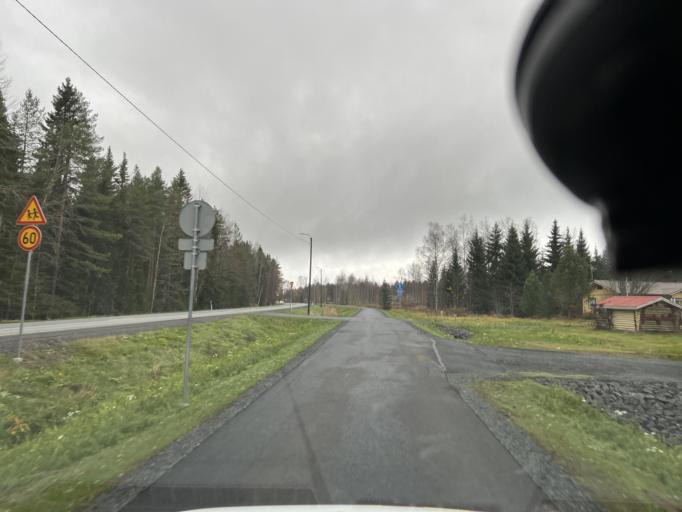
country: FI
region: Northern Ostrobothnia
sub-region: Ylivieska
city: Sievi
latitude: 63.9416
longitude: 24.5311
